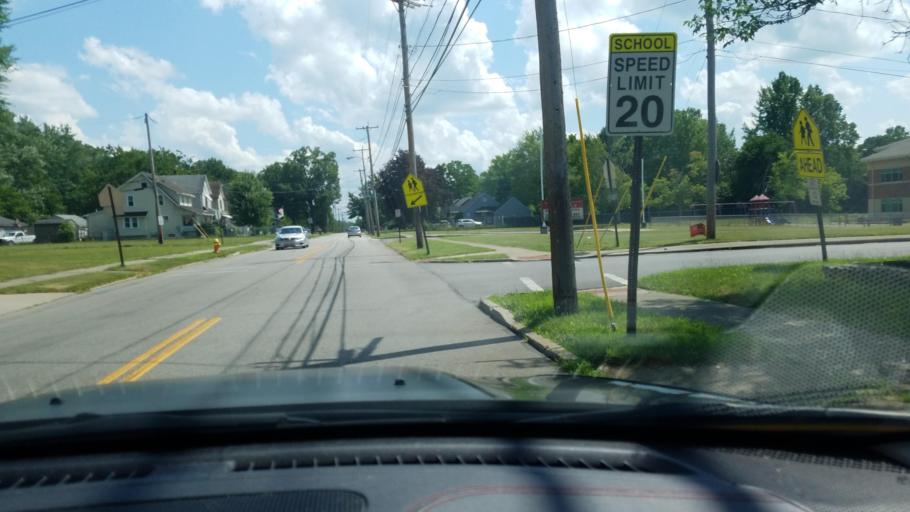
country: US
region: Ohio
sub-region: Mahoning County
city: Youngstown
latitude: 41.0972
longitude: -80.6999
